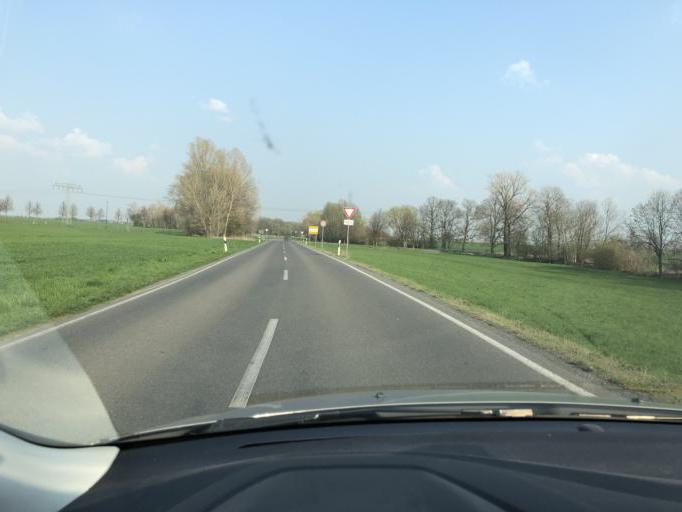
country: DE
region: Saxony
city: Rackwitz
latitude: 51.4349
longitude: 12.3853
